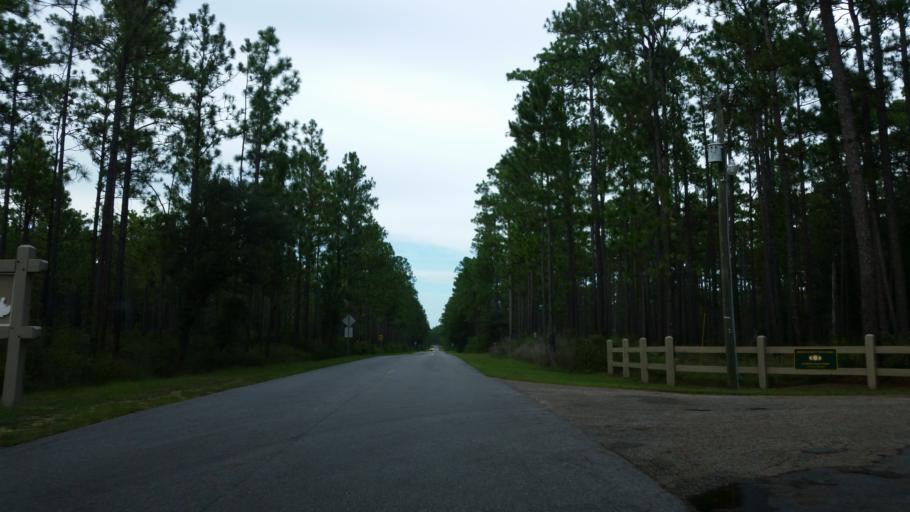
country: US
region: Florida
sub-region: Santa Rosa County
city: East Milton
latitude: 30.7118
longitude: -86.8801
